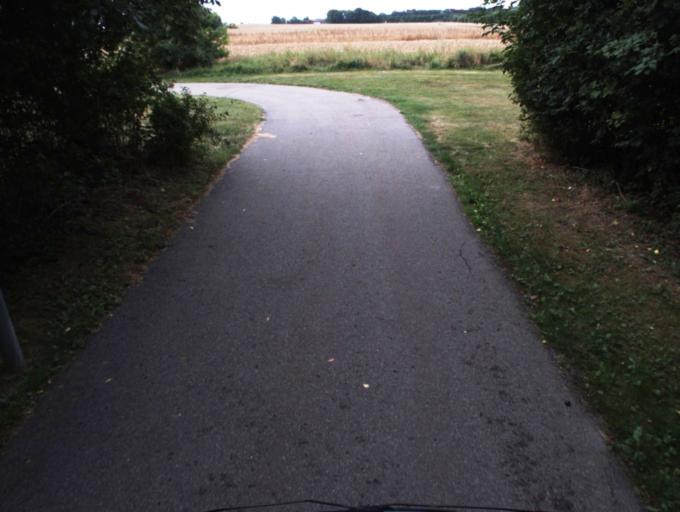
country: SE
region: Skane
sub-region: Helsingborg
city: Morarp
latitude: 56.0527
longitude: 12.8756
